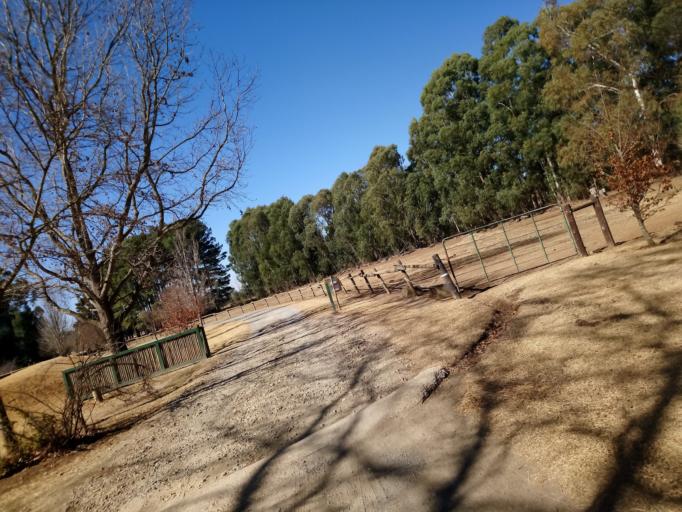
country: ZA
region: KwaZulu-Natal
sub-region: uMgungundlovu District Municipality
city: Mooirivier
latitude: -29.3233
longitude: 29.7160
